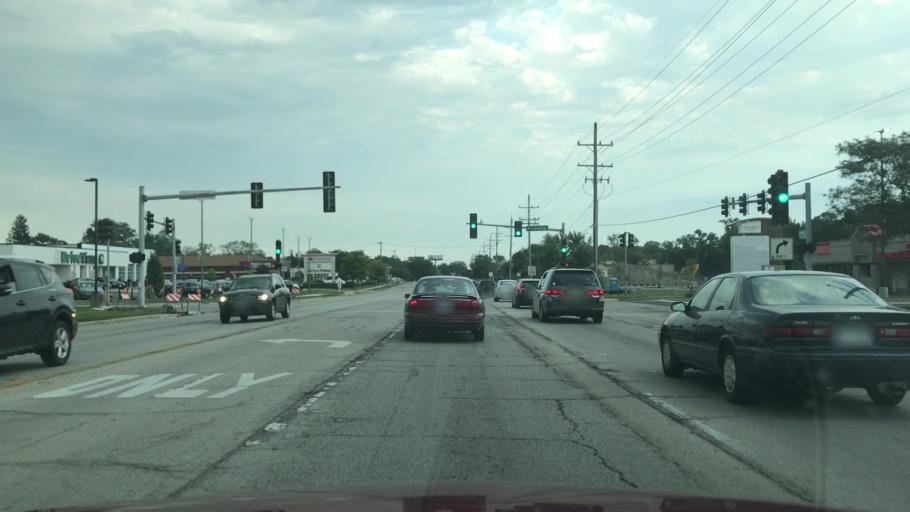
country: US
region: Illinois
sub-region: DuPage County
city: Lombard
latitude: 41.8604
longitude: -88.0054
